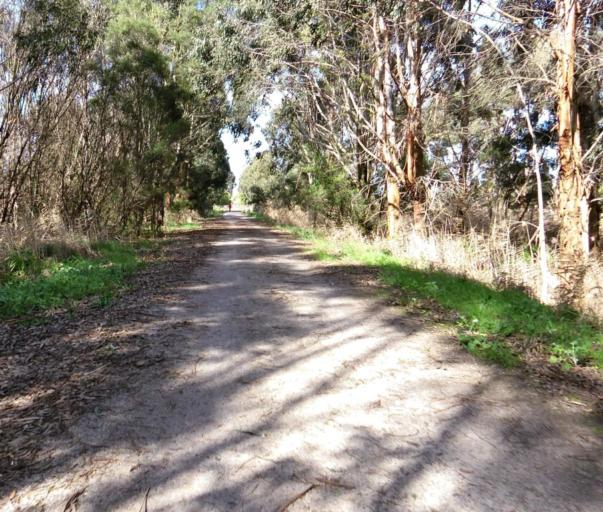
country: AU
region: Victoria
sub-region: Baw Baw
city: Warragul
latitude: -38.4953
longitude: 145.9403
